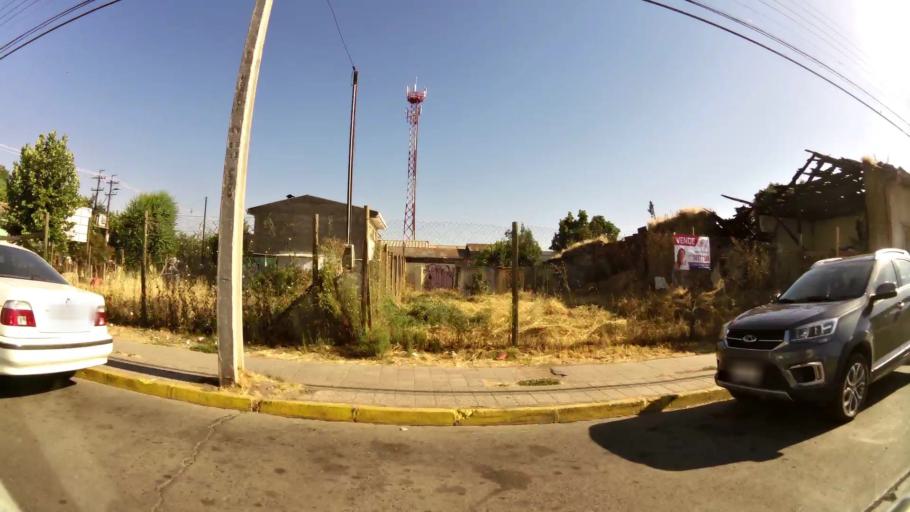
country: CL
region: Maule
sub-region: Provincia de Curico
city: Curico
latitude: -34.9874
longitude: -71.2438
